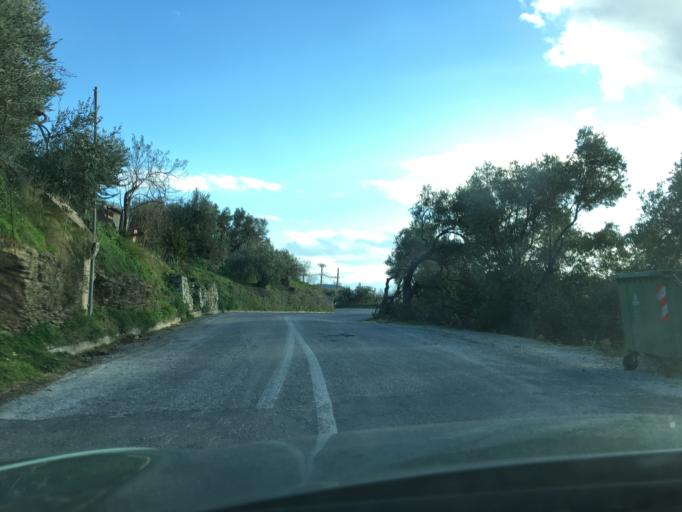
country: GR
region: Thessaly
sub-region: Nomos Magnisias
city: Skopelos
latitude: 39.1684
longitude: 23.6174
